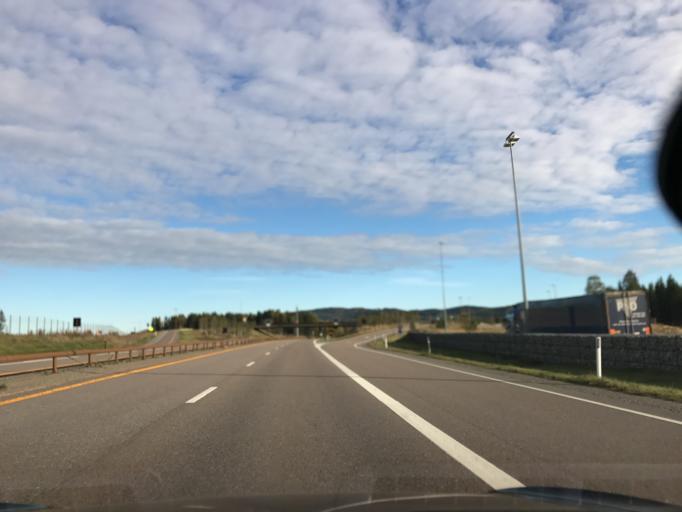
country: NO
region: Akershus
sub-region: Eidsvoll
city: Eidsvoll
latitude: 60.3873
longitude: 11.2136
